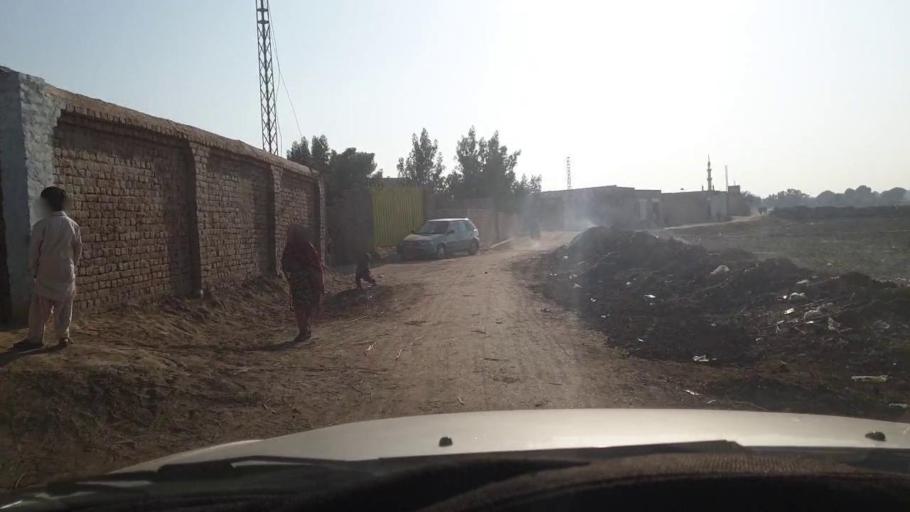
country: PK
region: Sindh
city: Mirpur Mathelo
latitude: 28.0206
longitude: 69.6049
